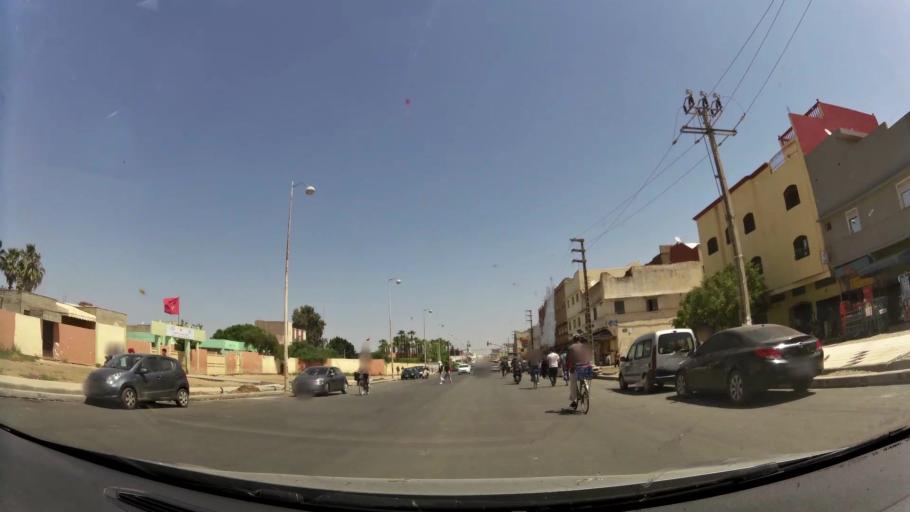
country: MA
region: Rabat-Sale-Zemmour-Zaer
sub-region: Khemisset
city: Khemisset
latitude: 33.8220
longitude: -6.0721
